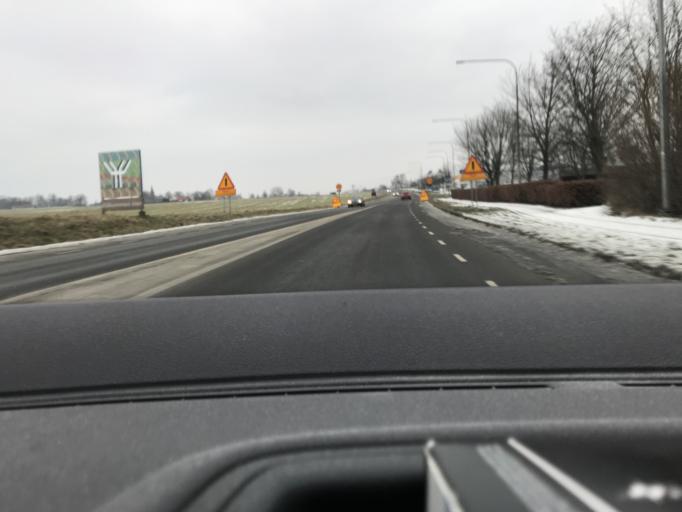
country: SE
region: Skane
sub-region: Ystads Kommun
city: Ystad
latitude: 55.4446
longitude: 13.8369
